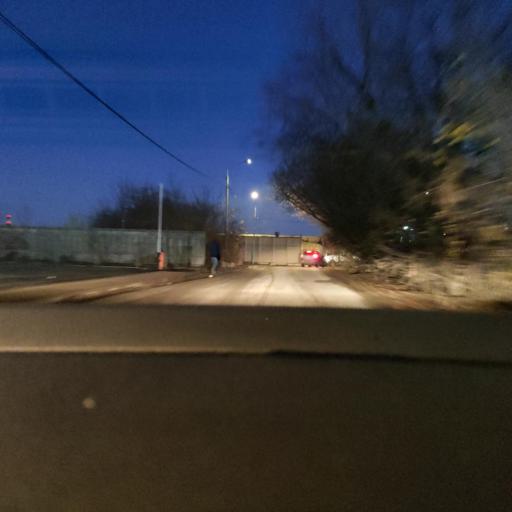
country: RU
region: Moscow
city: Kapotnya
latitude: 55.6586
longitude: 37.8002
